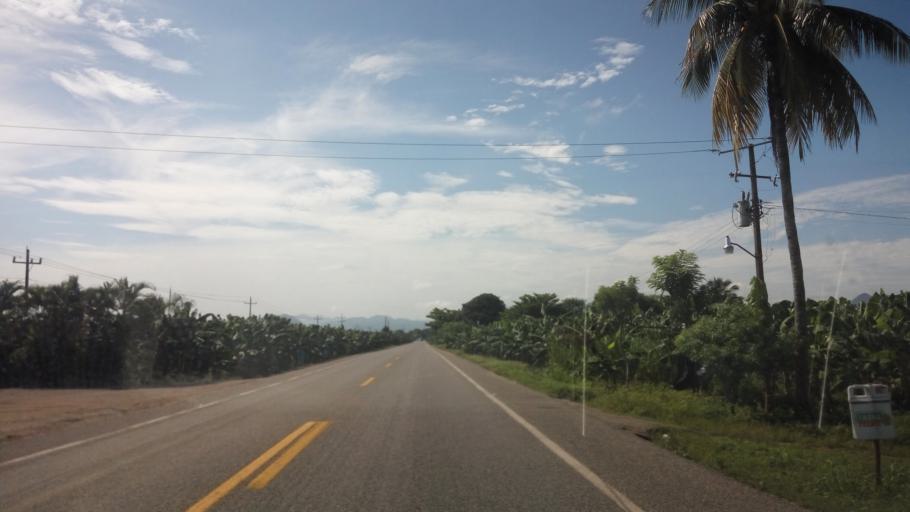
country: MX
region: Tabasco
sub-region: Teapa
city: Eureka y Belen
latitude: 17.6374
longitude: -92.9674
